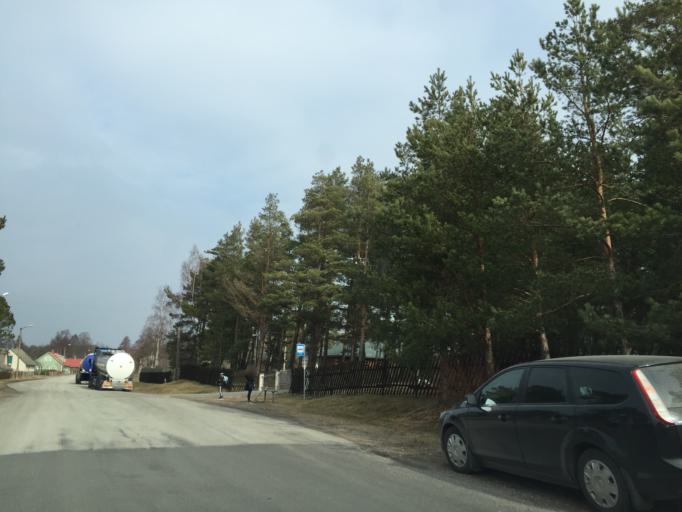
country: LV
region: Salacgrivas
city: Ainazi
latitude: 57.9177
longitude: 24.3866
